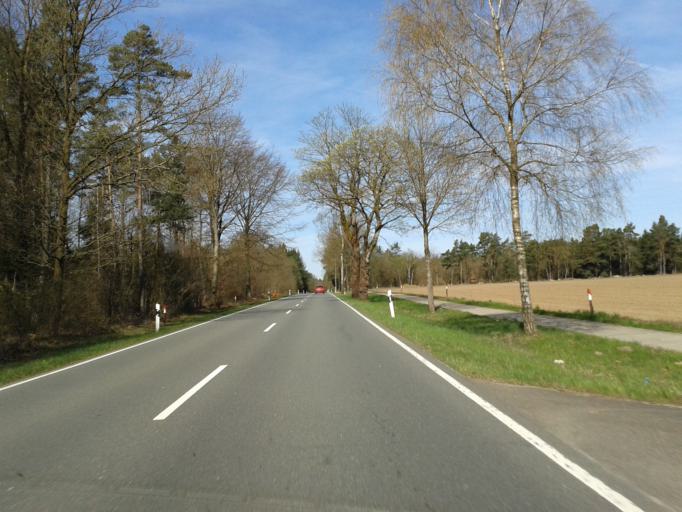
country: DE
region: Lower Saxony
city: Eimke
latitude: 52.9738
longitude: 10.2699
